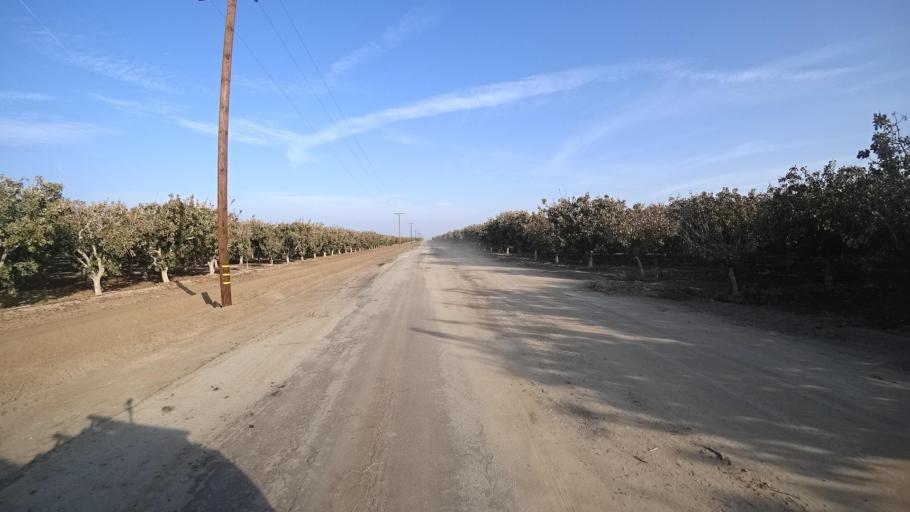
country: US
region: California
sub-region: Kern County
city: McFarland
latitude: 35.7285
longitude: -119.1873
